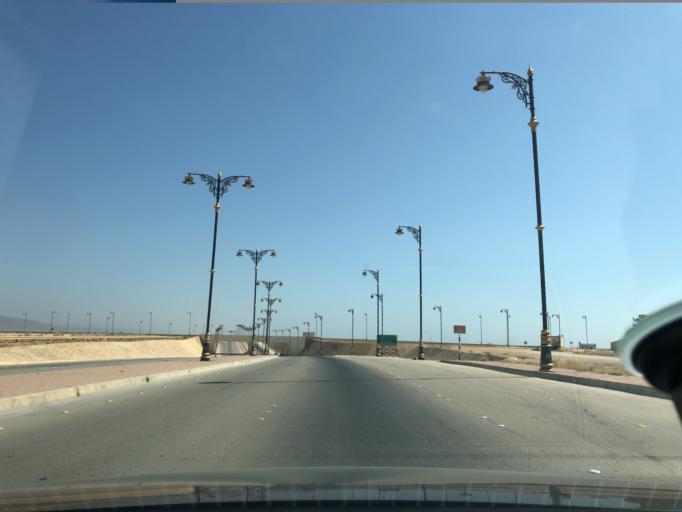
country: OM
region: Zufar
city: Salalah
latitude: 17.0505
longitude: 54.2217
